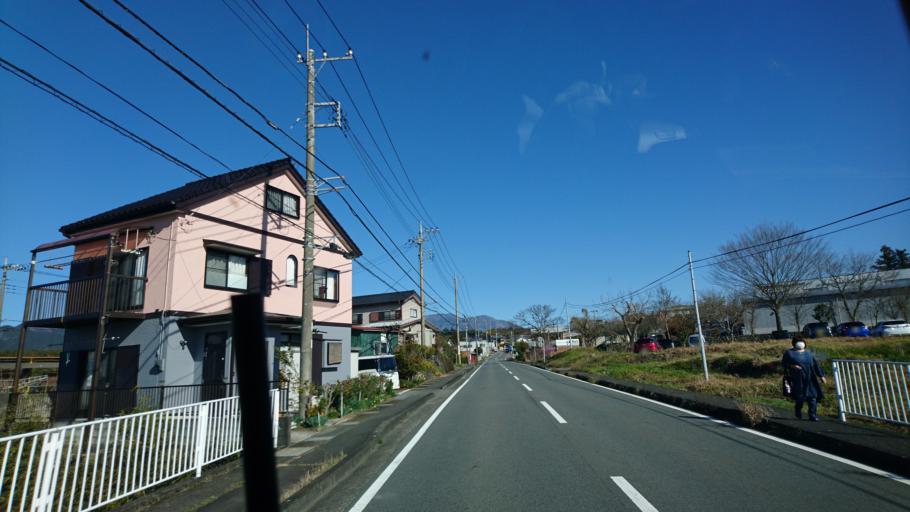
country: JP
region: Shizuoka
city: Fujinomiya
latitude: 35.2829
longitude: 138.6030
